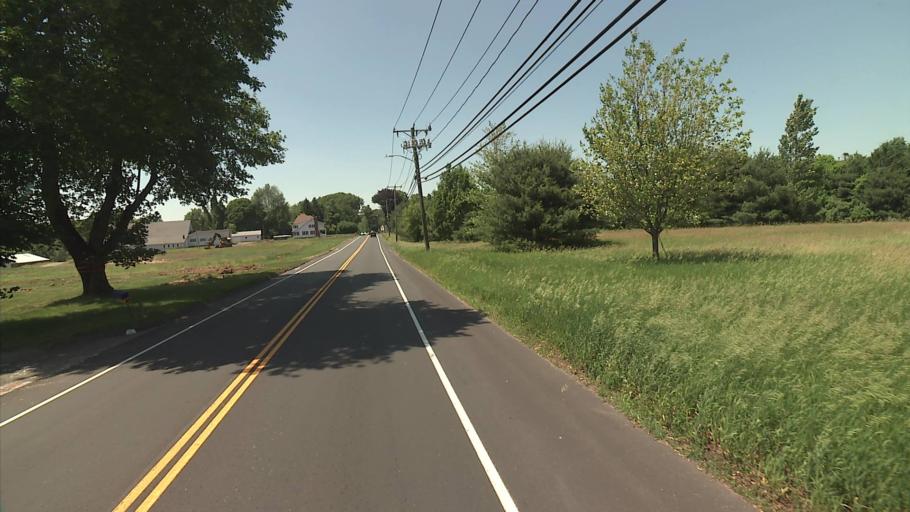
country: US
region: Connecticut
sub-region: Hartford County
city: Manchester
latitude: 41.8233
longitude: -72.5453
